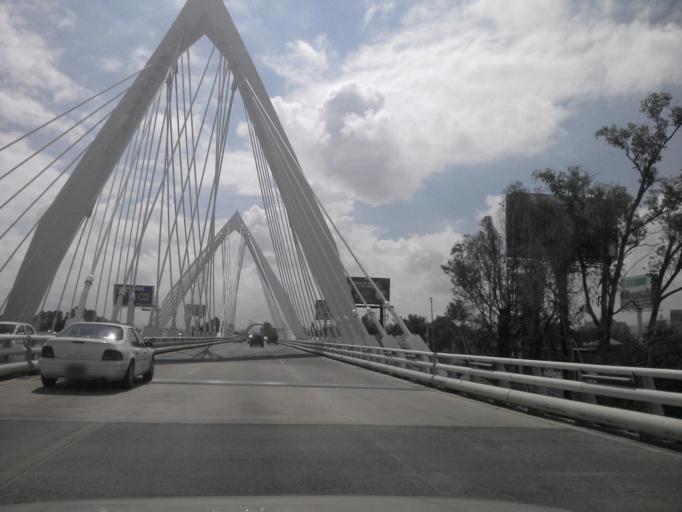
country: MX
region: Jalisco
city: Guadalajara
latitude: 20.6653
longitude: -103.3947
